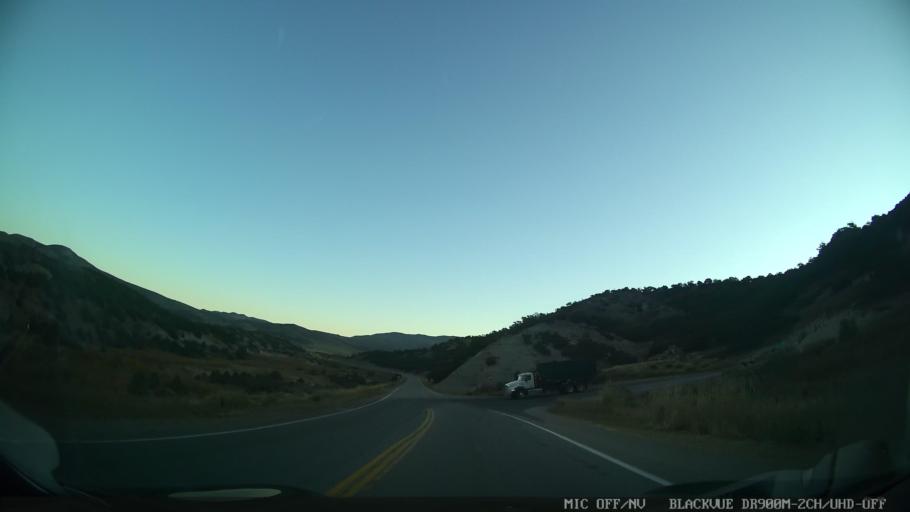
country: US
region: Colorado
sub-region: Eagle County
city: Edwards
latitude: 39.7223
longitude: -106.6793
